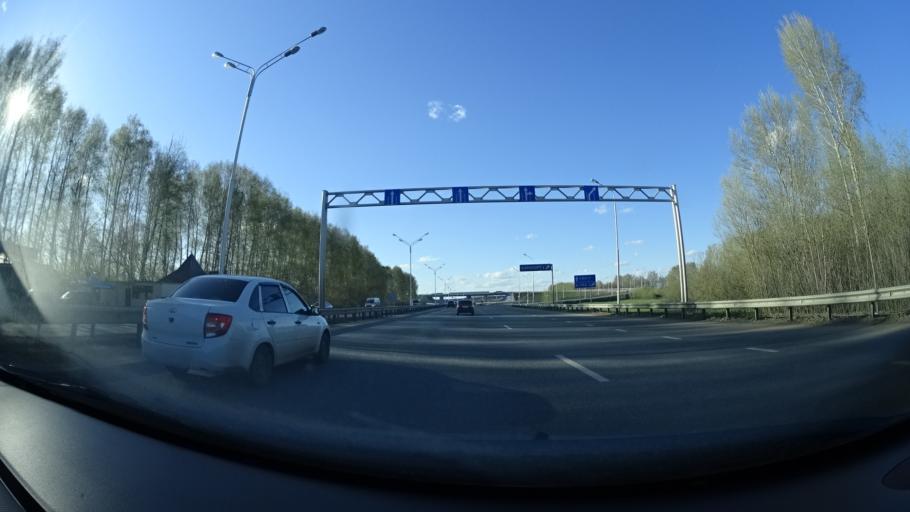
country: RU
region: Bashkortostan
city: Ufa
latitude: 54.5707
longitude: 55.9151
